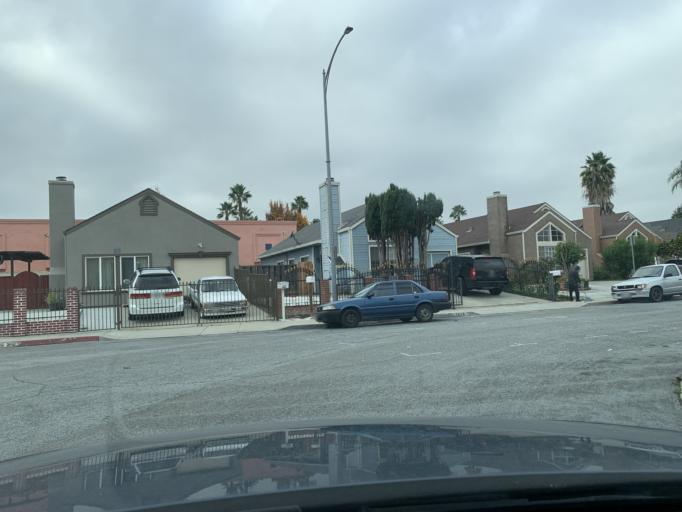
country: US
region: California
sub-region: Santa Clara County
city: Alum Rock
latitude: 37.3424
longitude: -121.8419
